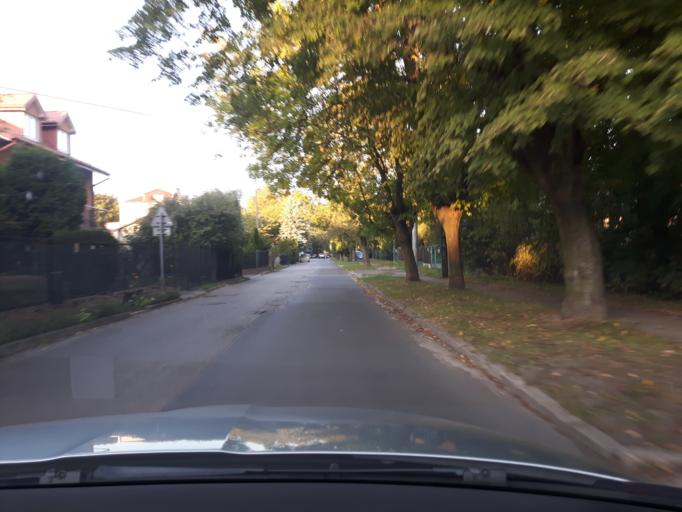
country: PL
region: Masovian Voivodeship
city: Zielonka
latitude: 52.3029
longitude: 21.1541
